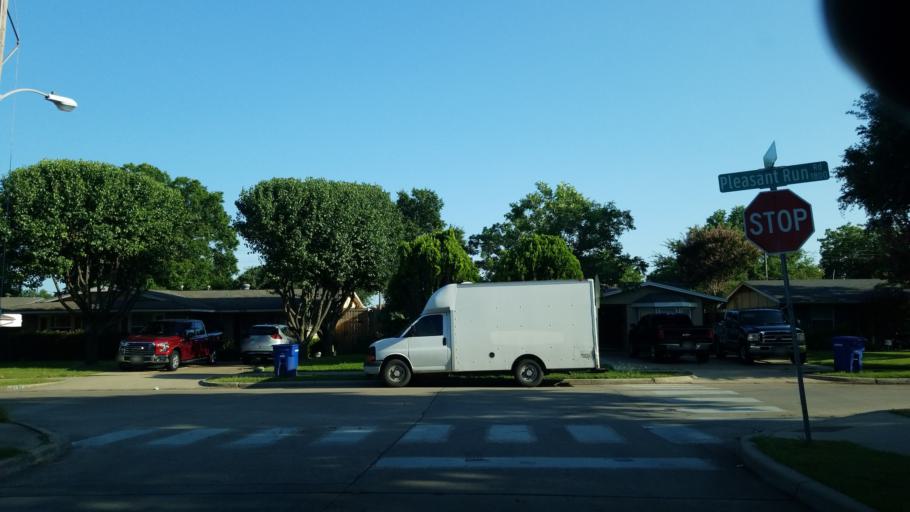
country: US
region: Texas
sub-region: Dallas County
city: Carrollton
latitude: 32.9443
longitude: -96.8931
